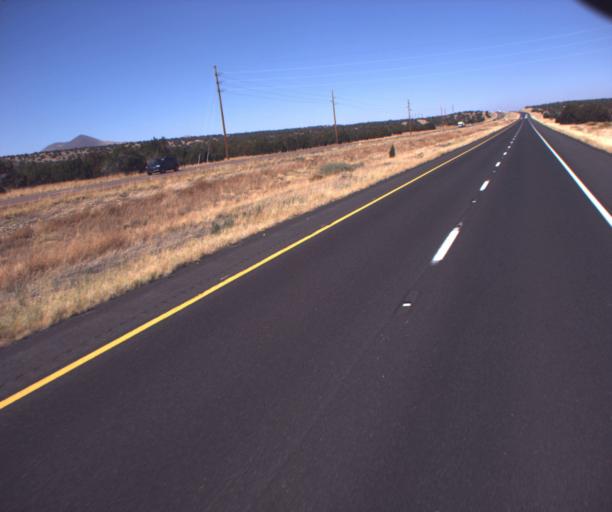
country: US
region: Arizona
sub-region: Coconino County
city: Flagstaff
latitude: 35.4592
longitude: -111.5607
